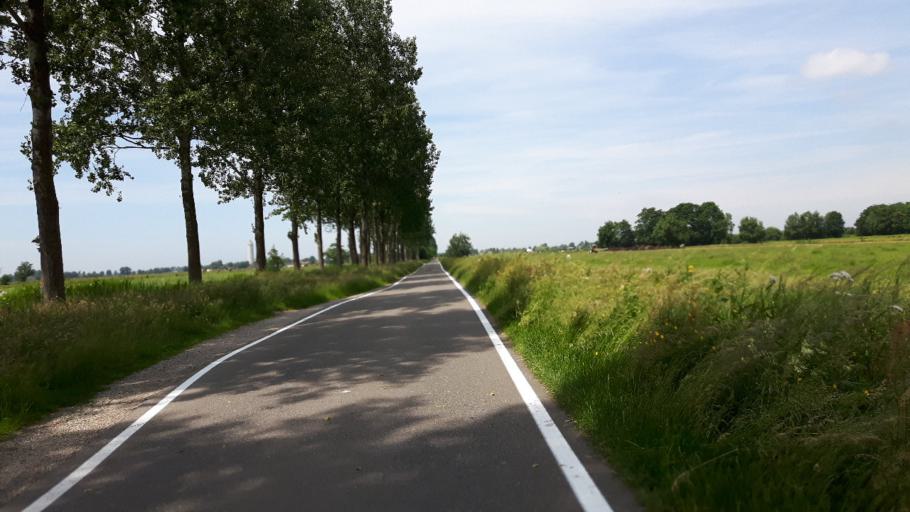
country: NL
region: South Holland
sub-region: Gemeente Nieuwkoop
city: Nieuwkoop
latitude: 52.1150
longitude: 4.8084
